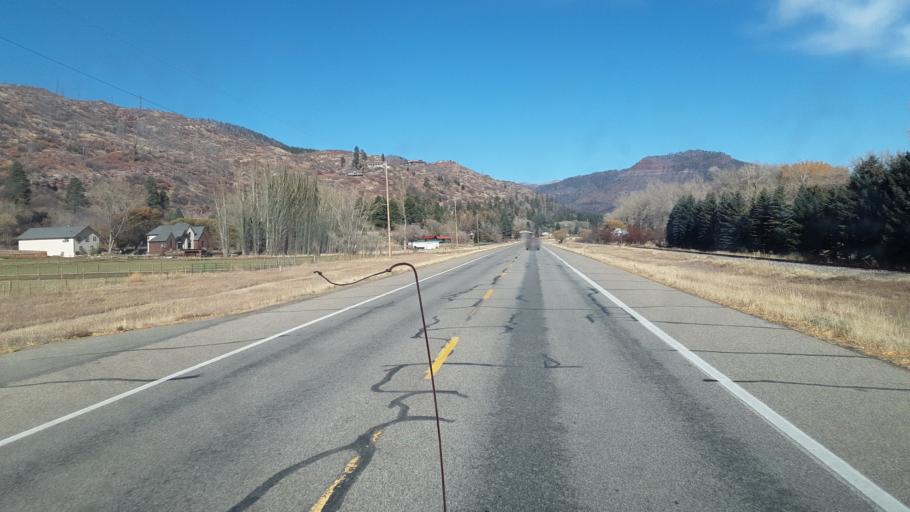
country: US
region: Colorado
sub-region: La Plata County
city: Durango
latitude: 37.3771
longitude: -107.8511
